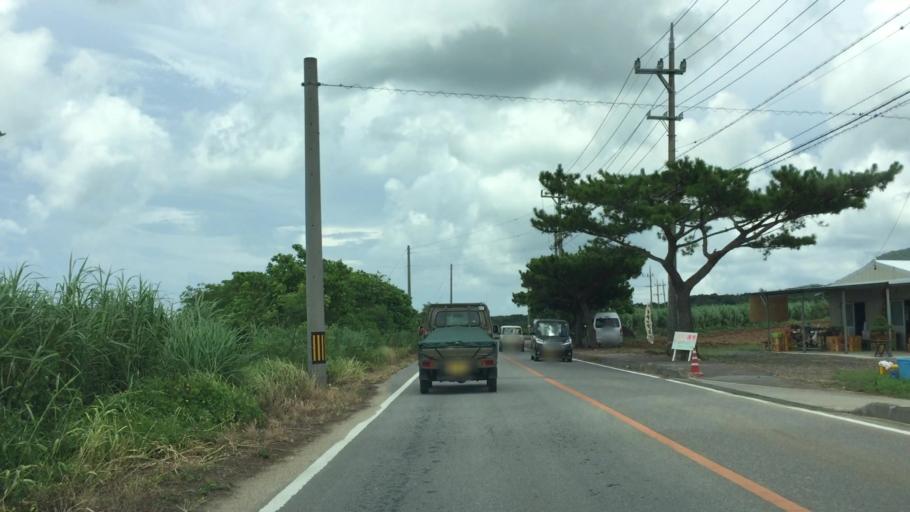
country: JP
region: Okinawa
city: Ishigaki
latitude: 24.3984
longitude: 124.1525
